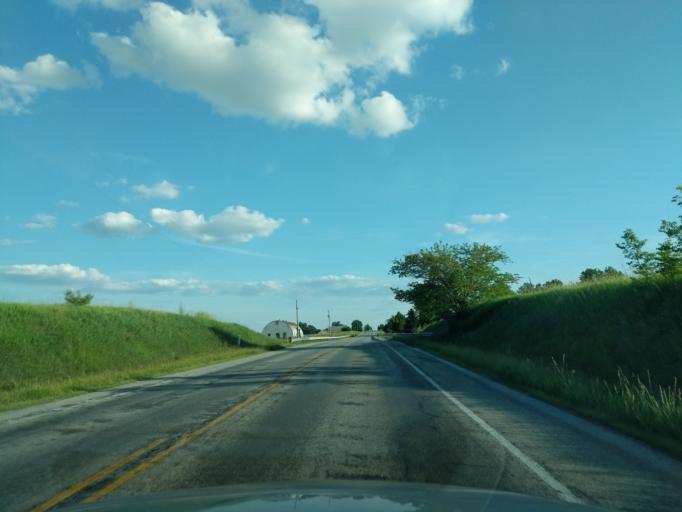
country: US
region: Indiana
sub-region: Huntington County
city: Huntington
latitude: 40.8201
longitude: -85.4654
